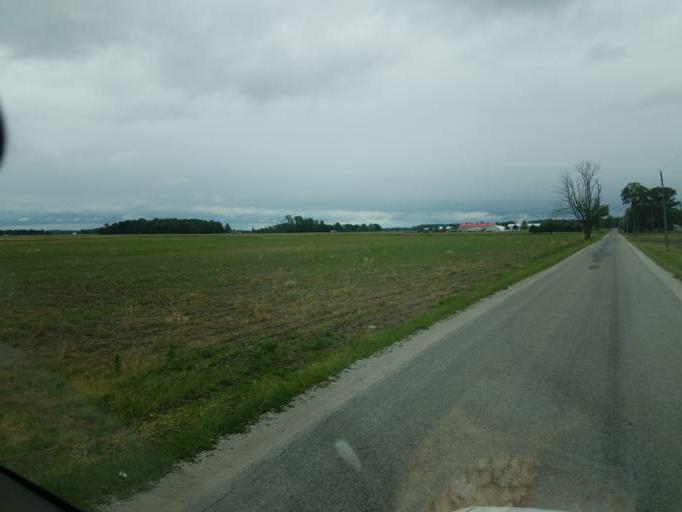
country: US
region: Ohio
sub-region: Marion County
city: Marion
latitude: 40.5596
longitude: -83.0680
